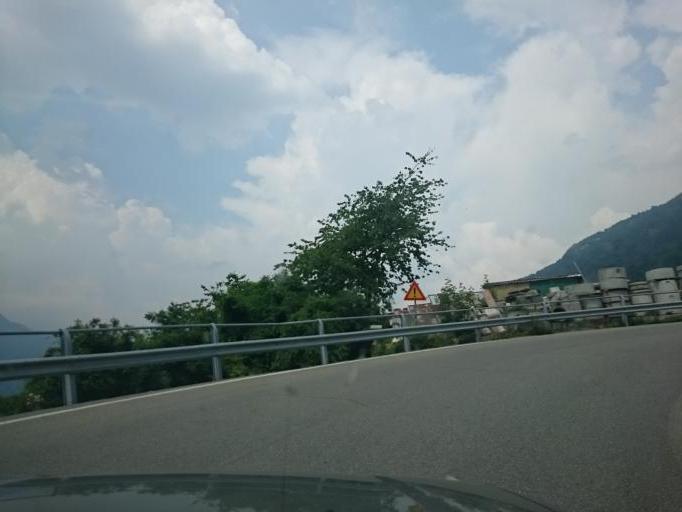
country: IT
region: Lombardy
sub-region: Provincia di Brescia
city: Cimbergo
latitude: 46.0260
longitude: 10.3678
